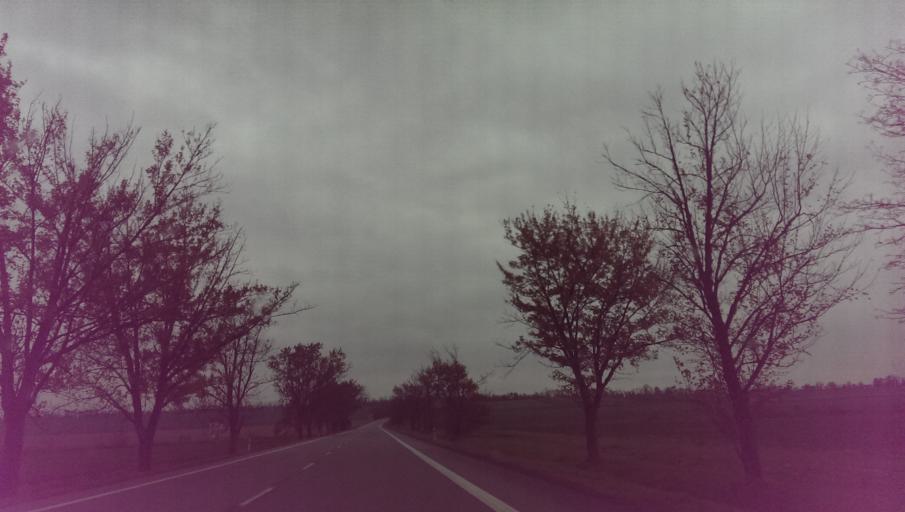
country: CZ
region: South Moravian
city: Olbramovice
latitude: 48.9629
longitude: 16.4421
